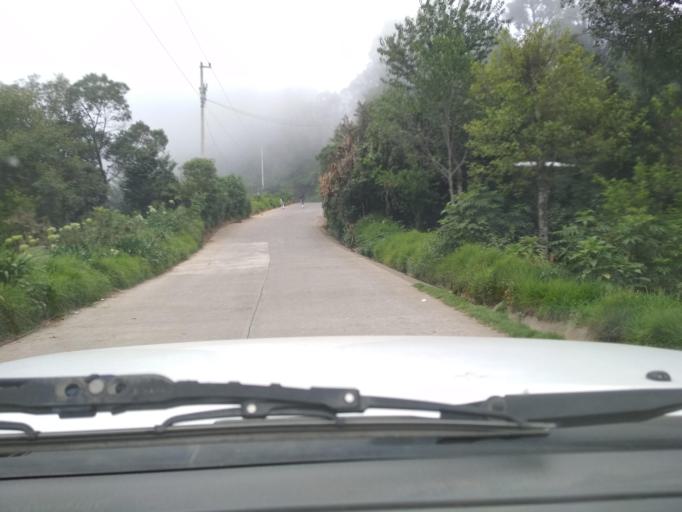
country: MX
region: Veracruz
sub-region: La Perla
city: Metlac Hernandez (Metlac Primero)
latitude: 18.9738
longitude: -97.1557
